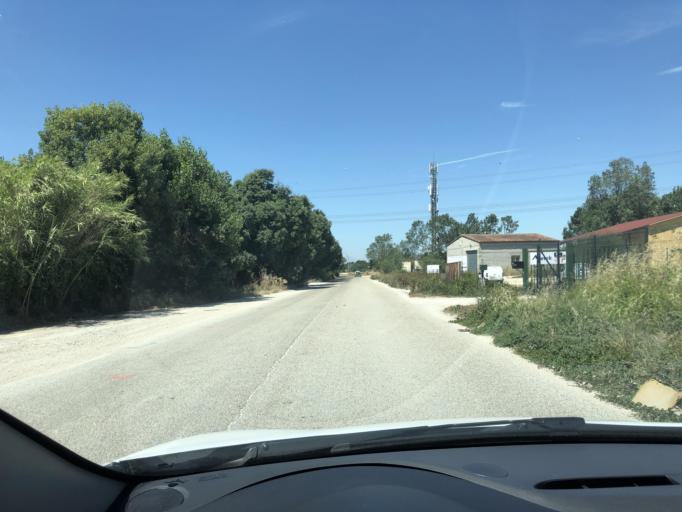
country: FR
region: Provence-Alpes-Cote d'Azur
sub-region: Departement des Bouches-du-Rhone
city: Chateaurenard
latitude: 43.9002
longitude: 4.8748
